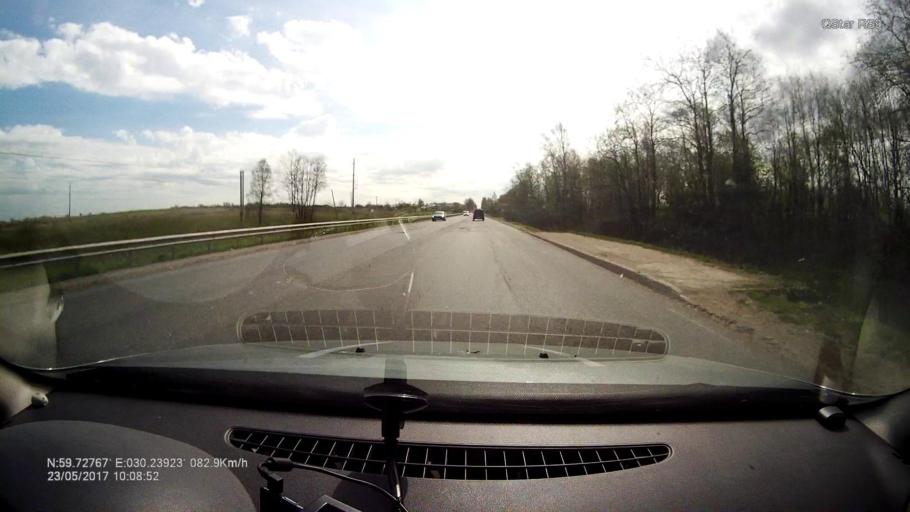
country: RU
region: St.-Petersburg
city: Aleksandrovskaya
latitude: 59.7276
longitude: 30.2396
